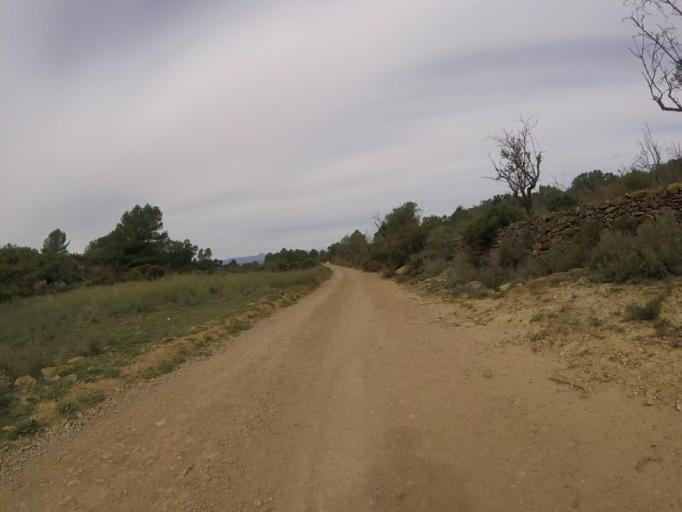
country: ES
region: Valencia
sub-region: Provincia de Castello
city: Cabanes
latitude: 40.1946
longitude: 0.0766
